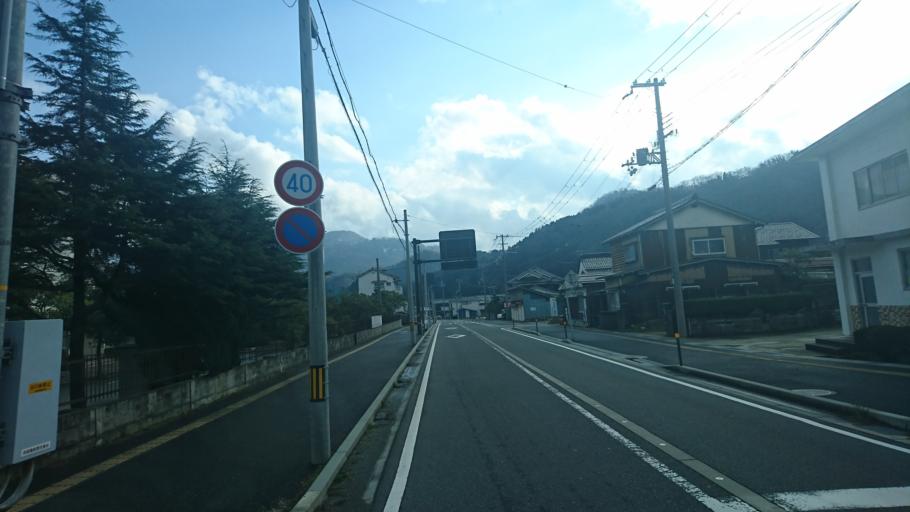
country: JP
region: Tottori
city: Tottori
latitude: 35.6270
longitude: 134.4454
